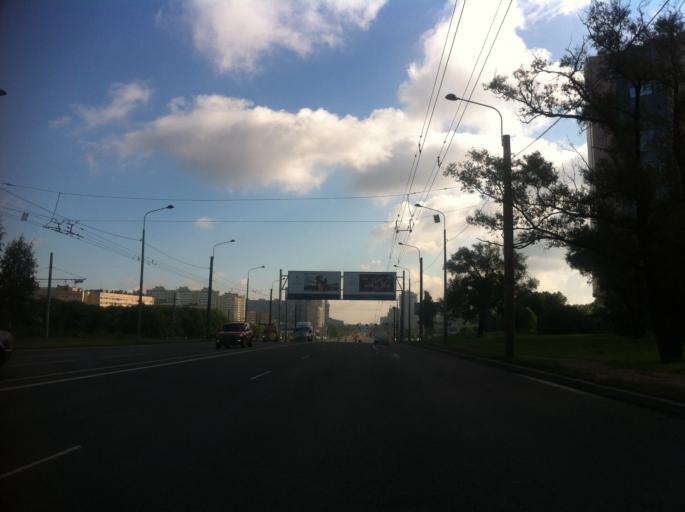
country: RU
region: St.-Petersburg
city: Uritsk
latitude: 59.8431
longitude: 30.2086
